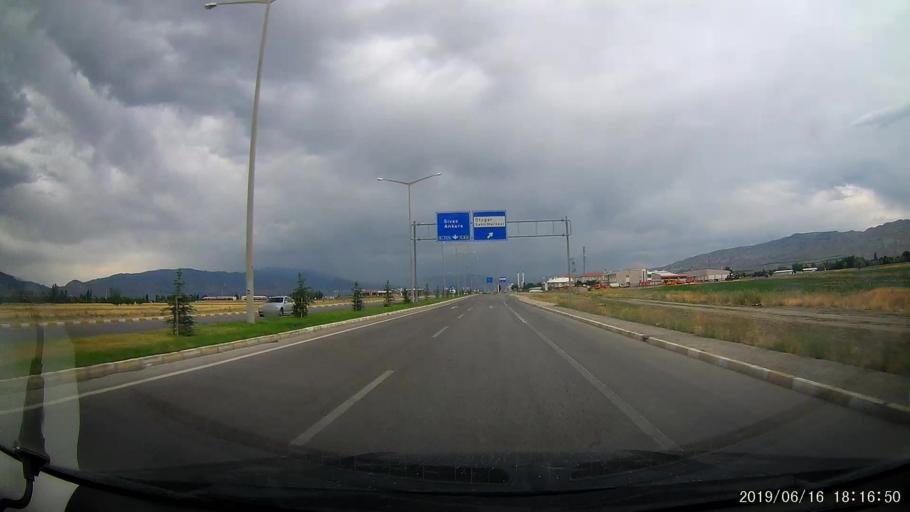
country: TR
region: Erzincan
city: Erzincan
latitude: 39.7307
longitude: 39.5421
